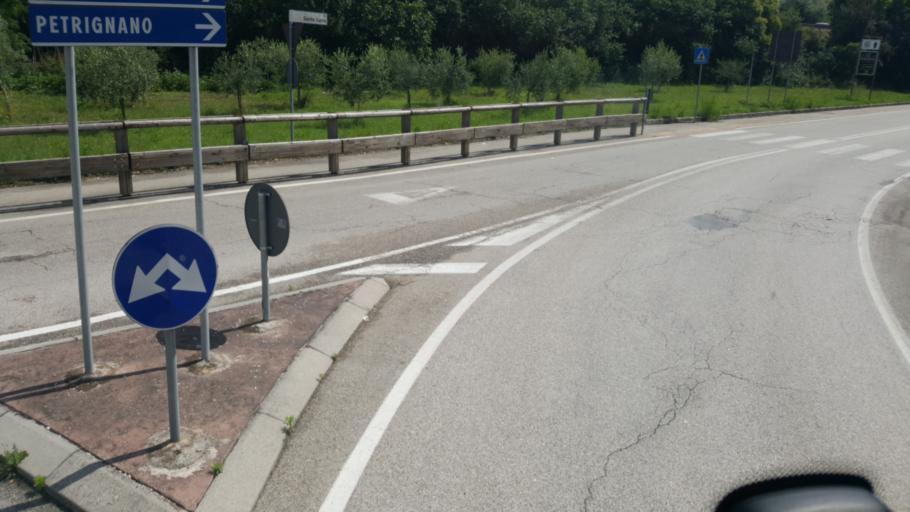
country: IT
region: Umbria
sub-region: Provincia di Perugia
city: Bastia umbra
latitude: 43.0665
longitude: 12.5353
